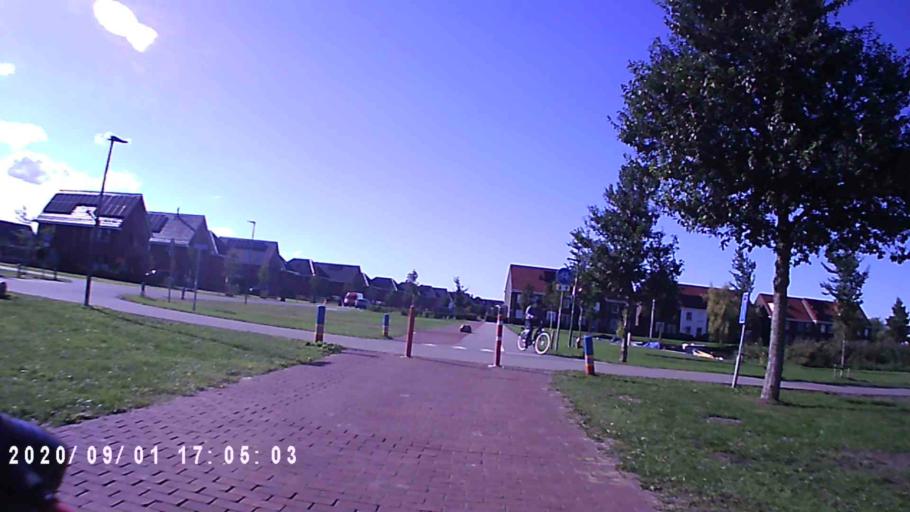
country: NL
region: Groningen
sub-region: Gemeente Haren
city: Haren
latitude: 53.2196
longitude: 6.6561
